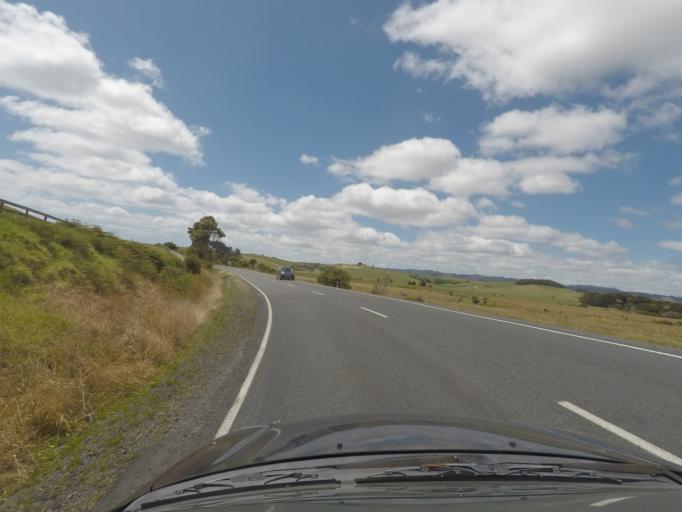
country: NZ
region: Northland
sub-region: Whangarei
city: Ruakaka
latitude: -35.9898
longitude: 174.4566
